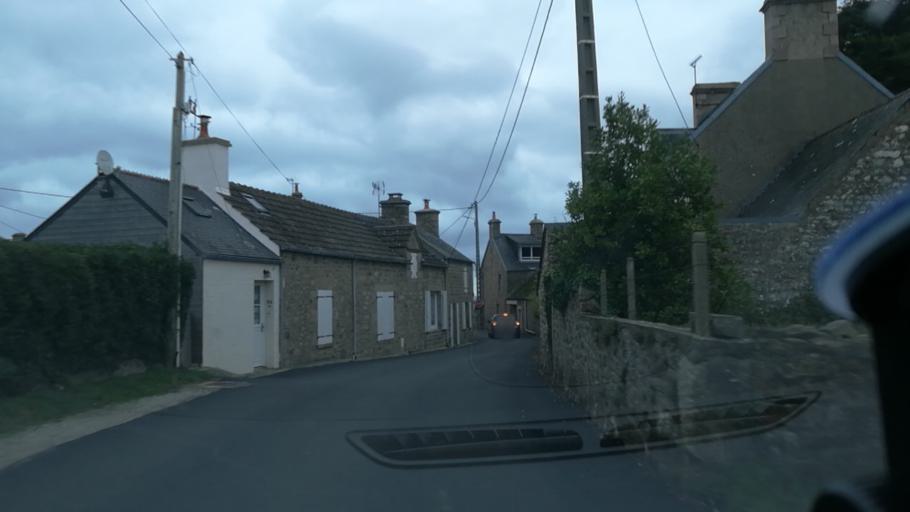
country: FR
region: Lower Normandy
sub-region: Departement de la Manche
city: Fermanville
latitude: 49.6843
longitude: -1.4567
